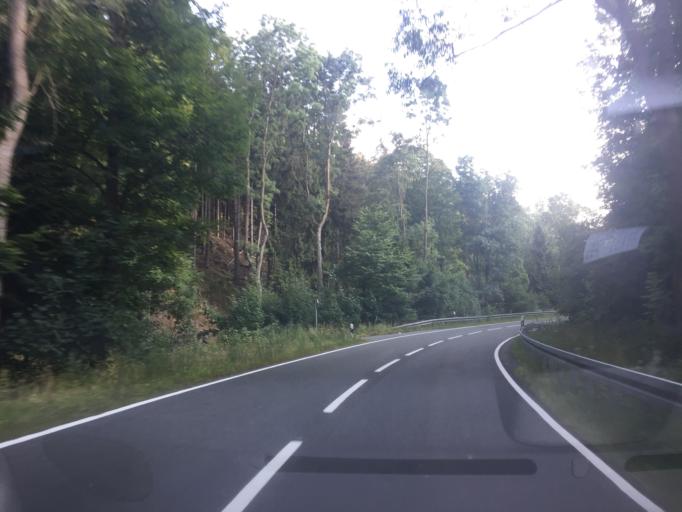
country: DE
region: Saxony-Anhalt
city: Darlingerode
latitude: 51.7925
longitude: 10.7384
